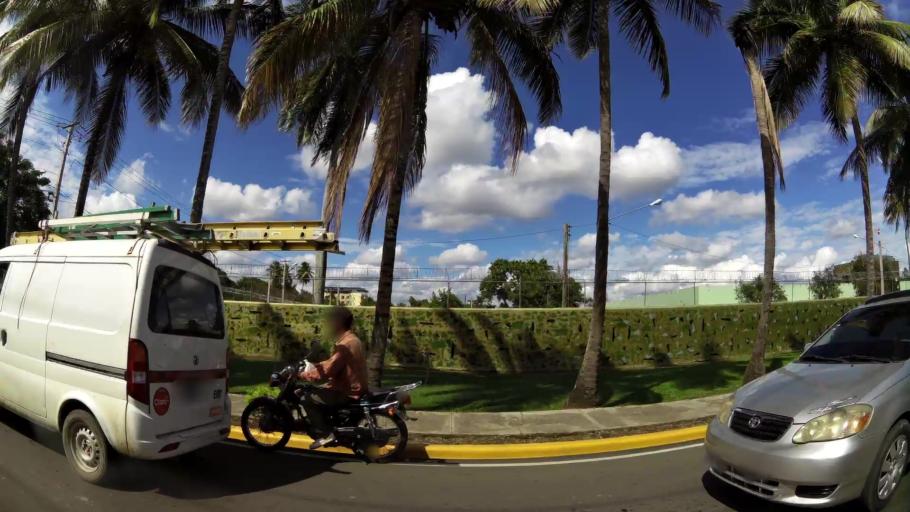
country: DO
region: La Vega
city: Concepcion de La Vega
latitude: 19.2196
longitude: -70.5203
